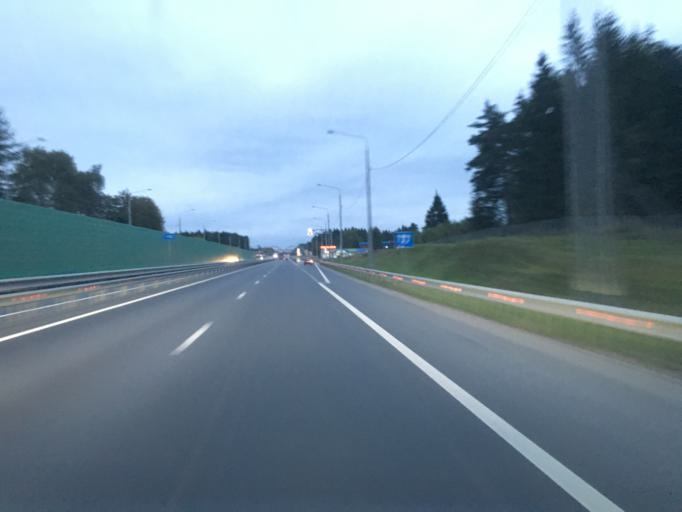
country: RU
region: Kaluga
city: Maloyaroslavets
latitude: 54.9200
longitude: 36.3978
